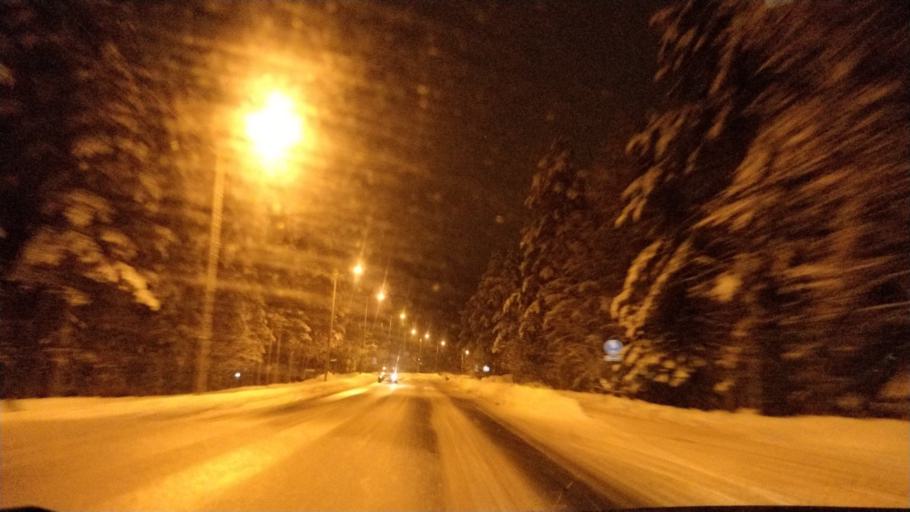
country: FI
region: Lapland
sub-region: Rovaniemi
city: Rovaniemi
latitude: 66.3785
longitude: 25.3811
